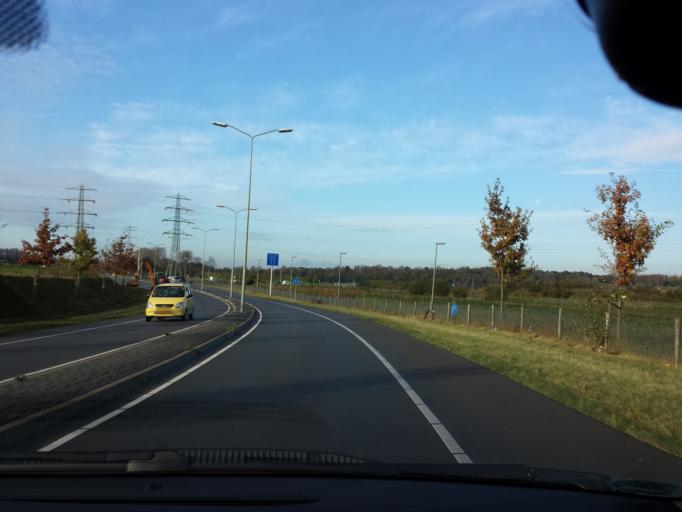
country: NL
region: Limburg
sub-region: Gemeente Heerlen
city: Heerlen
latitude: 50.9071
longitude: 5.9908
